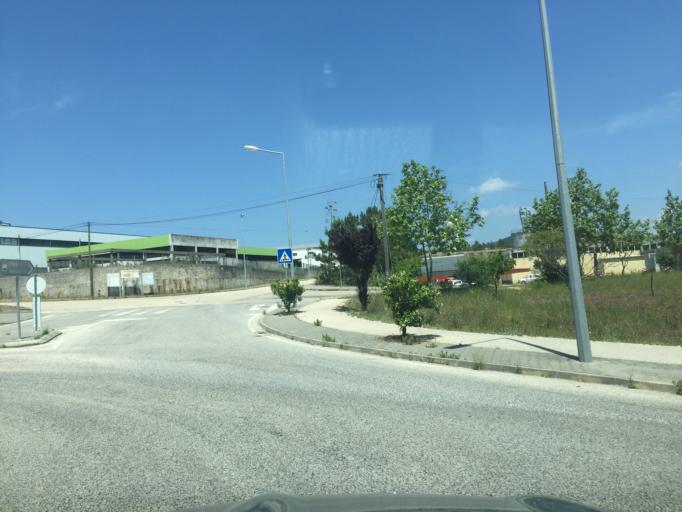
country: PT
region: Castelo Branco
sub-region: Vila de Rei
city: Vila de Rei
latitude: 39.6763
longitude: -8.1396
